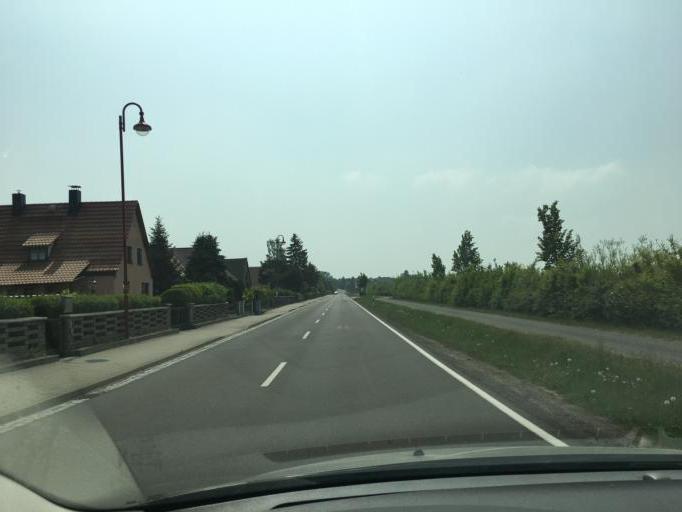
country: DE
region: Saxony
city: Grossposna
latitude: 51.2800
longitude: 12.5046
